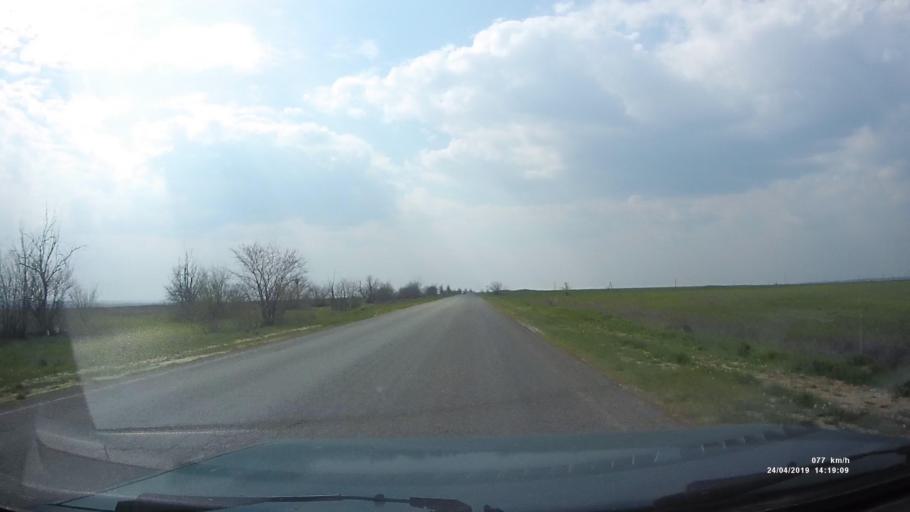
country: RU
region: Kalmykiya
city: Arshan'
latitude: 46.3046
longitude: 44.1807
